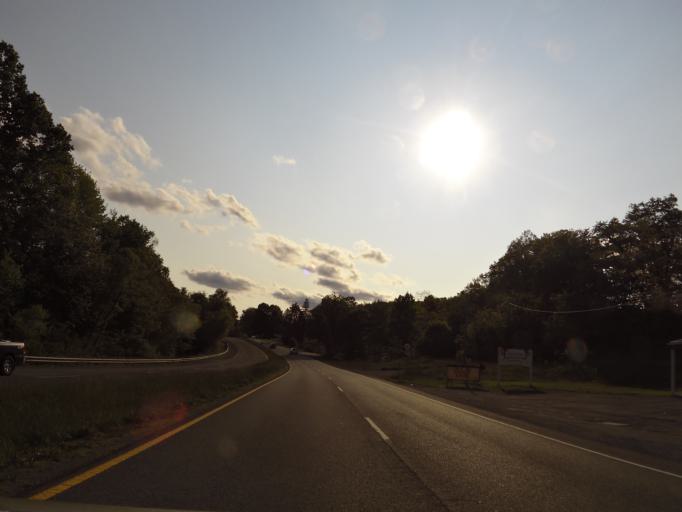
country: US
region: Virginia
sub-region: Tazewell County
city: Springville
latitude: 37.2164
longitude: -81.3568
